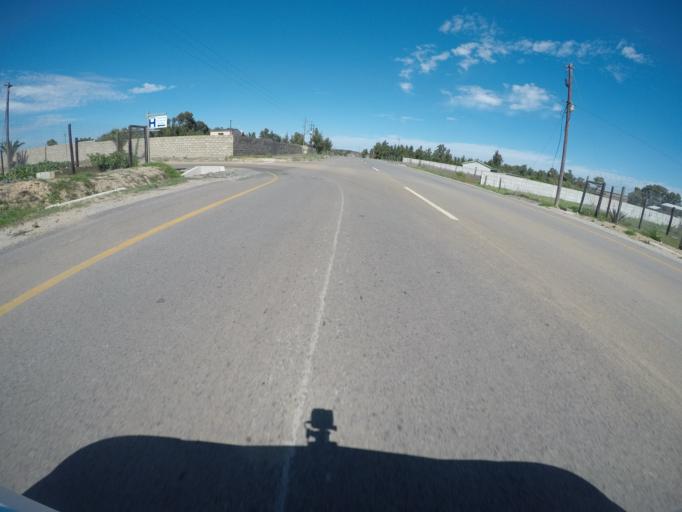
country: ZA
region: Western Cape
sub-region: West Coast District Municipality
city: Malmesbury
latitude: -33.5776
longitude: 18.6469
